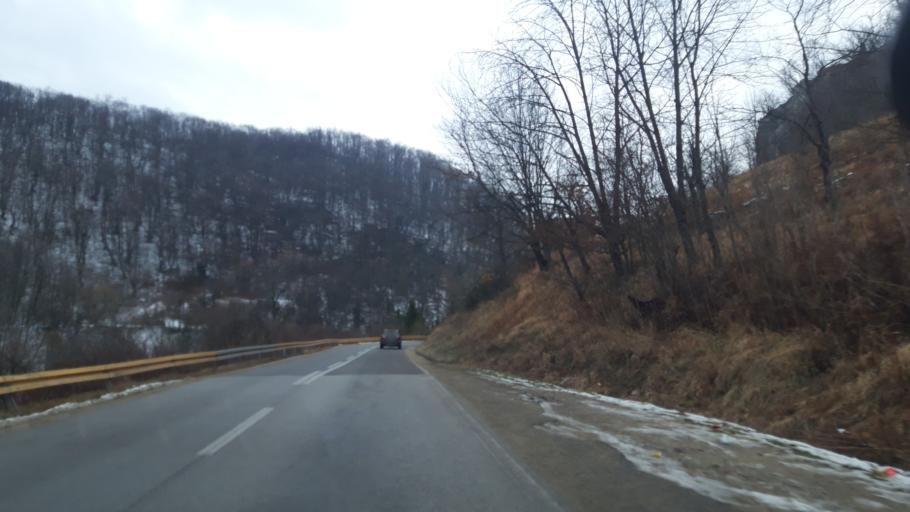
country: BA
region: Republika Srpska
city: Vlasenica
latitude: 44.1812
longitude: 18.9770
